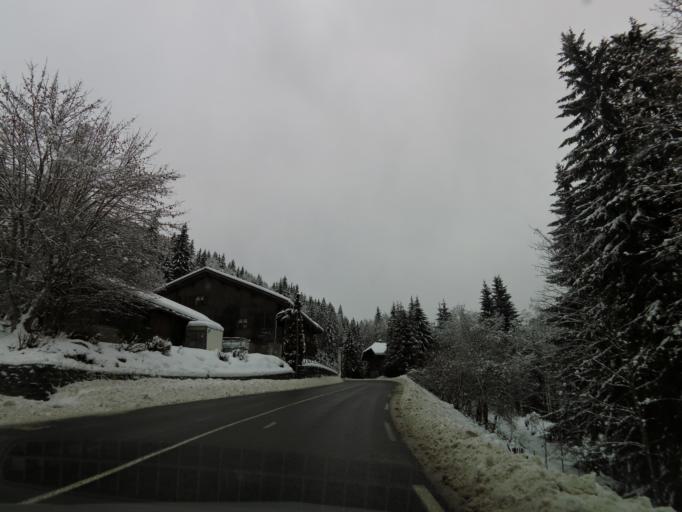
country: FR
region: Rhone-Alpes
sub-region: Departement de la Haute-Savoie
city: Morzine
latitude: 46.1795
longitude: 6.6833
